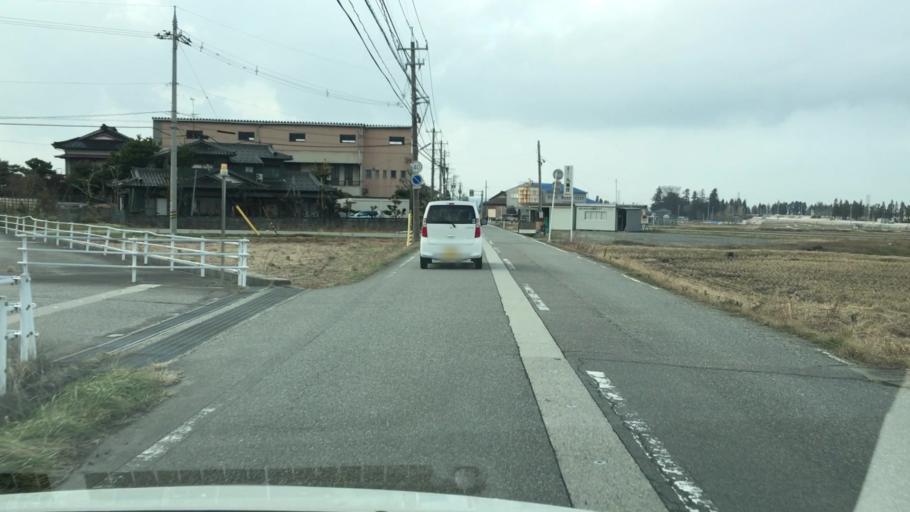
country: JP
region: Toyama
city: Toyama-shi
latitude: 36.6597
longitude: 137.2744
